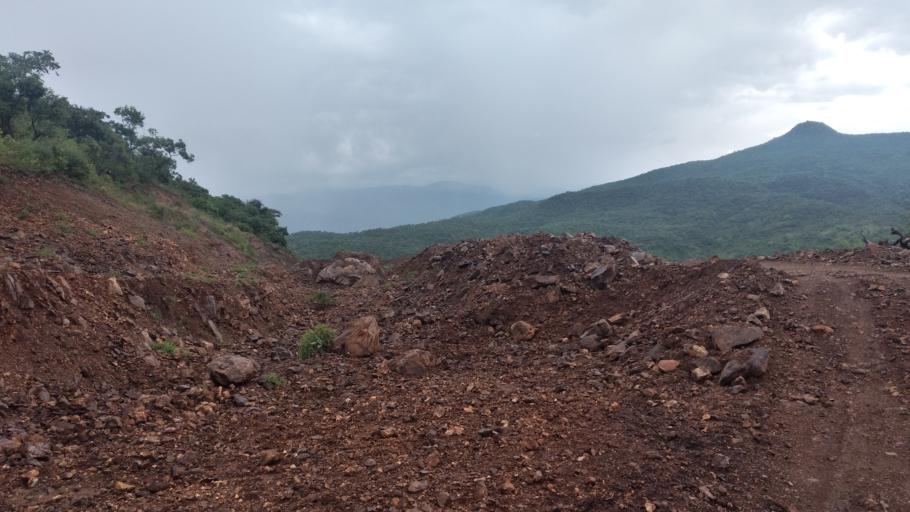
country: ET
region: Southern Nations, Nationalities, and People's Region
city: Areka
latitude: 7.6182
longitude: 37.5187
